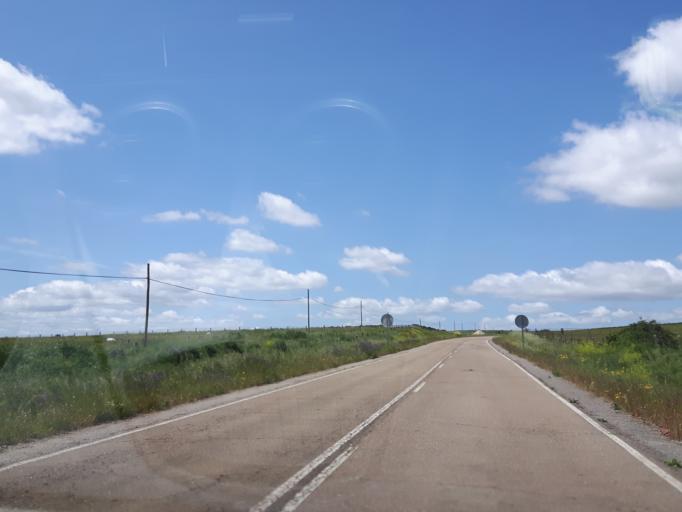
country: ES
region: Castille and Leon
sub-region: Provincia de Salamanca
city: Villar de Ciervo
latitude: 40.7322
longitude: -6.7452
